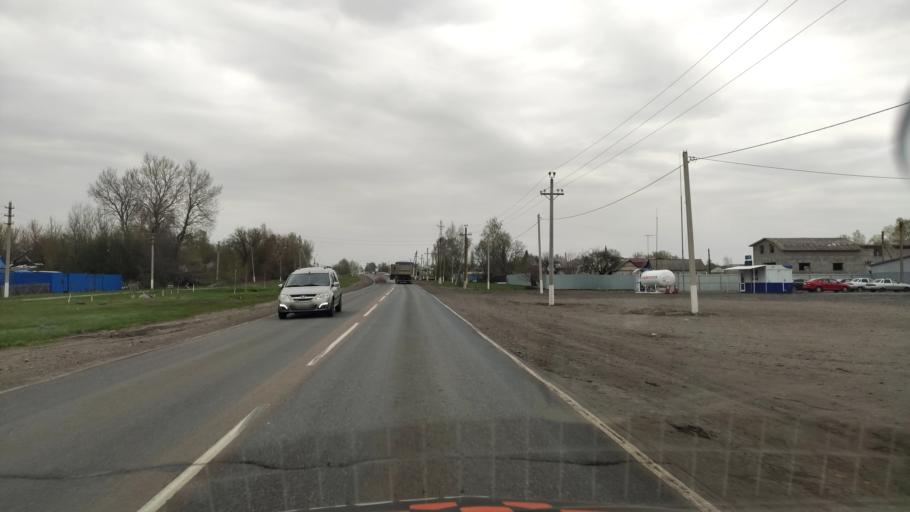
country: RU
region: Kursk
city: Gorshechnoye
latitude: 51.5165
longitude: 38.0121
